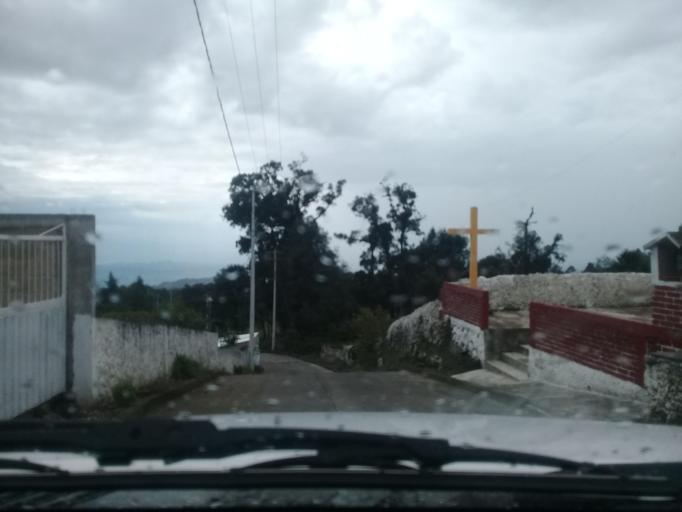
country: MX
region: Veracruz
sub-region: Acajete
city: La Joya
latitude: 19.6165
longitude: -97.0054
